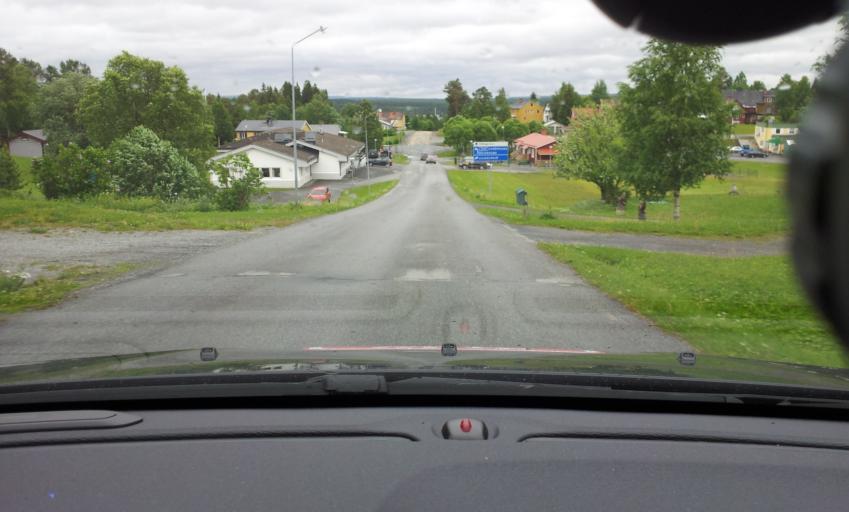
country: SE
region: Jaemtland
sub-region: Krokoms Kommun
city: Krokom
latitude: 63.6725
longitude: 14.6111
